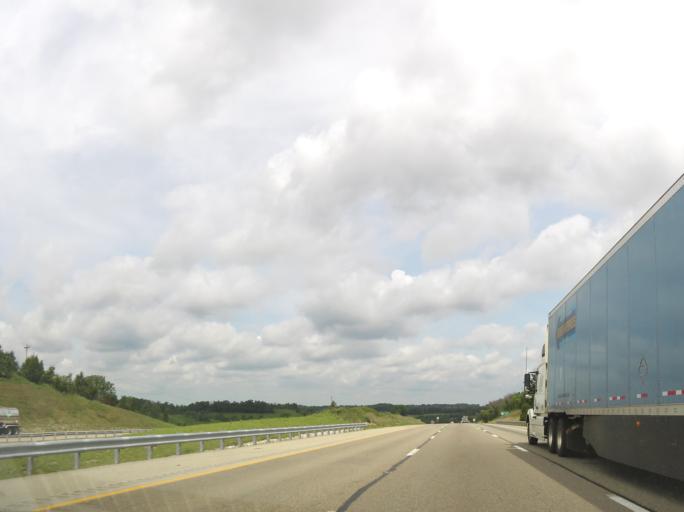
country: US
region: Kentucky
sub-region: Grant County
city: Williamstown
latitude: 38.4969
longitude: -84.5878
